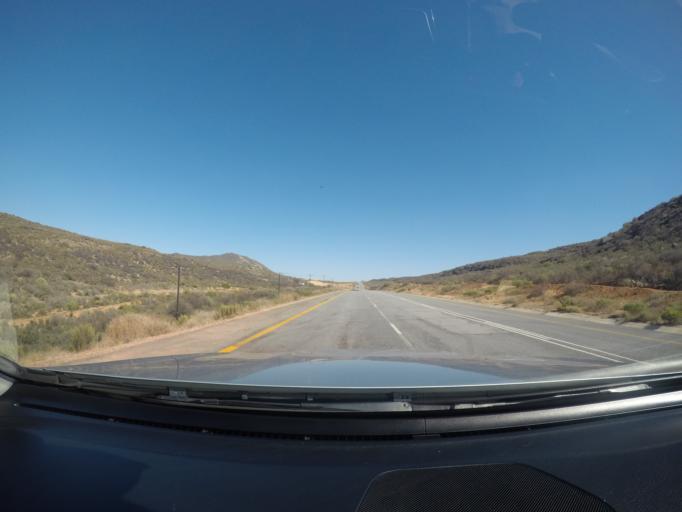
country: ZA
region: Western Cape
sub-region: West Coast District Municipality
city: Clanwilliam
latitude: -32.3036
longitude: 18.9054
